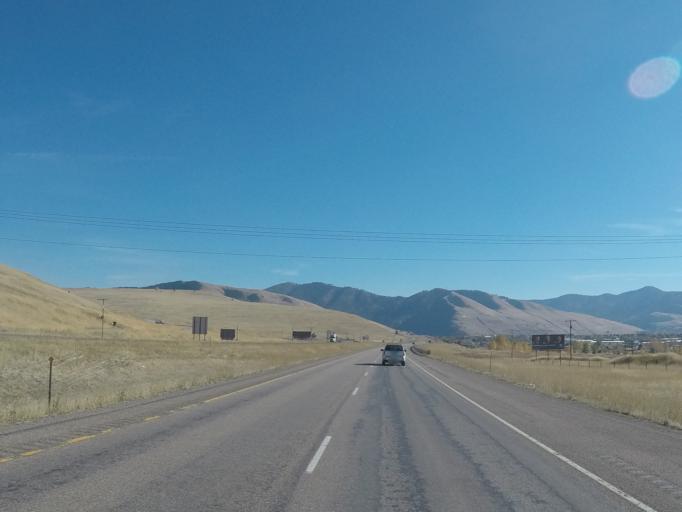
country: US
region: Montana
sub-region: Missoula County
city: Missoula
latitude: 46.9026
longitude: -114.0195
